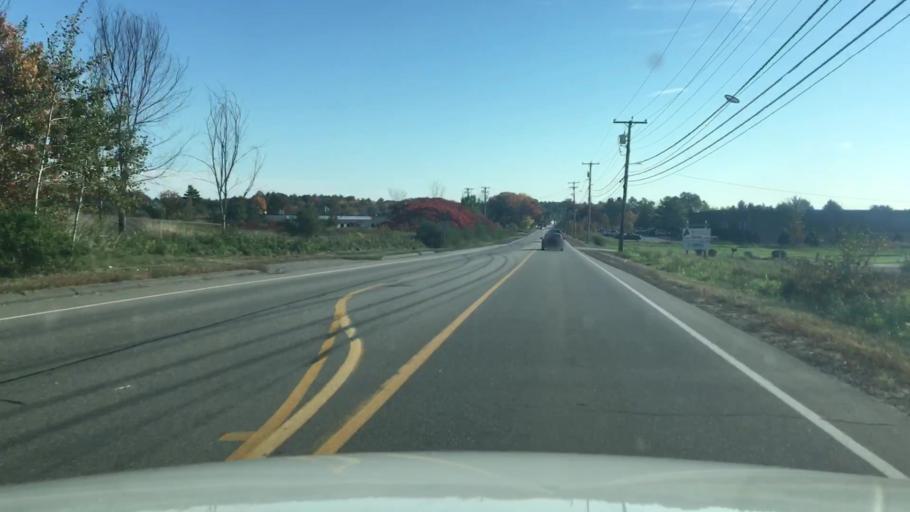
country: US
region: Maine
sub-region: Cumberland County
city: Westbrook
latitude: 43.6491
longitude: -70.3690
